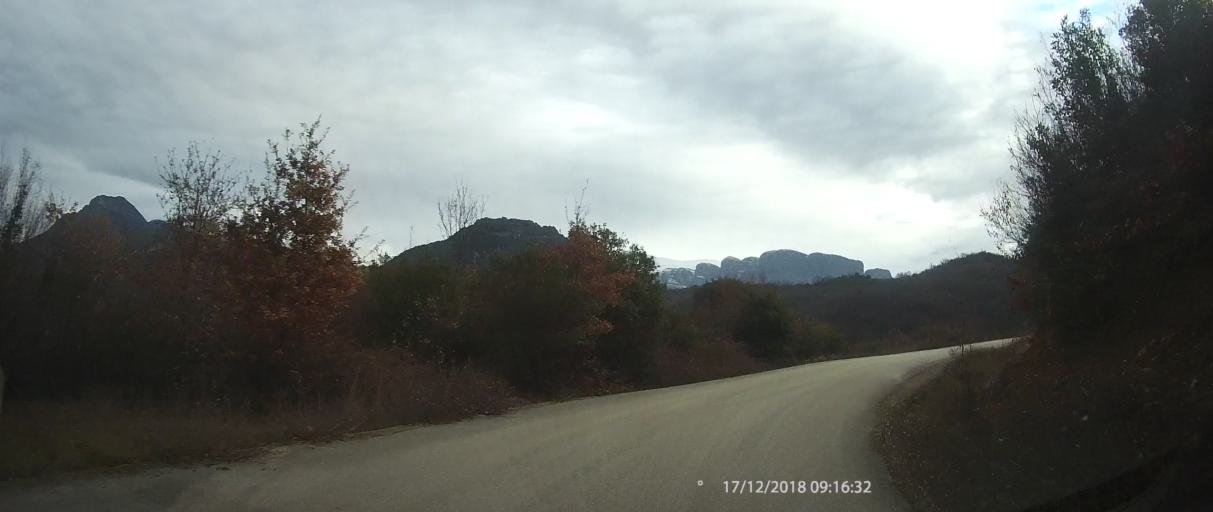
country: GR
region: Epirus
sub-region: Nomos Ioanninon
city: Kalpaki
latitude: 39.9613
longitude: 20.6584
